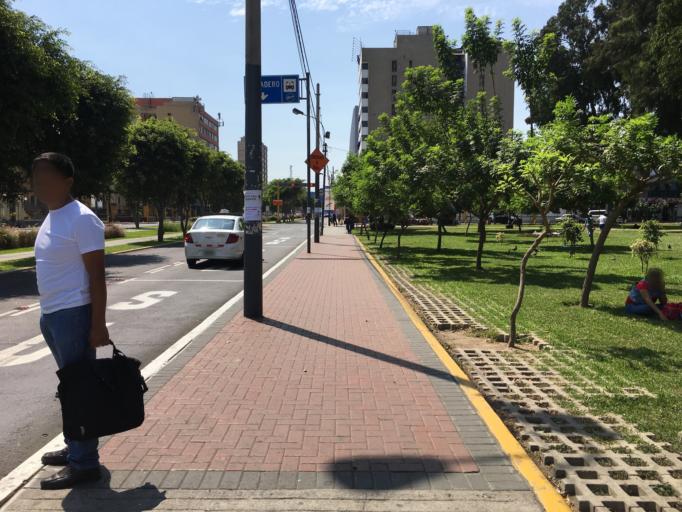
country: PE
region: Lima
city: Lima
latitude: -12.0690
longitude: -77.0367
